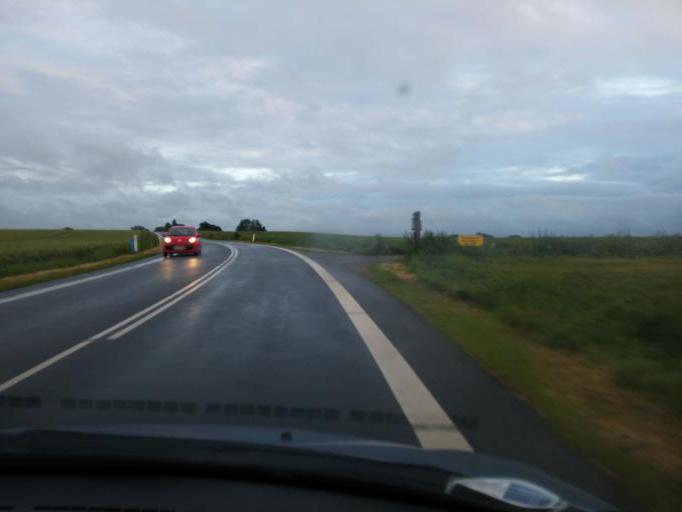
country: DK
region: South Denmark
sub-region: Kerteminde Kommune
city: Kerteminde
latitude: 55.4901
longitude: 10.6580
